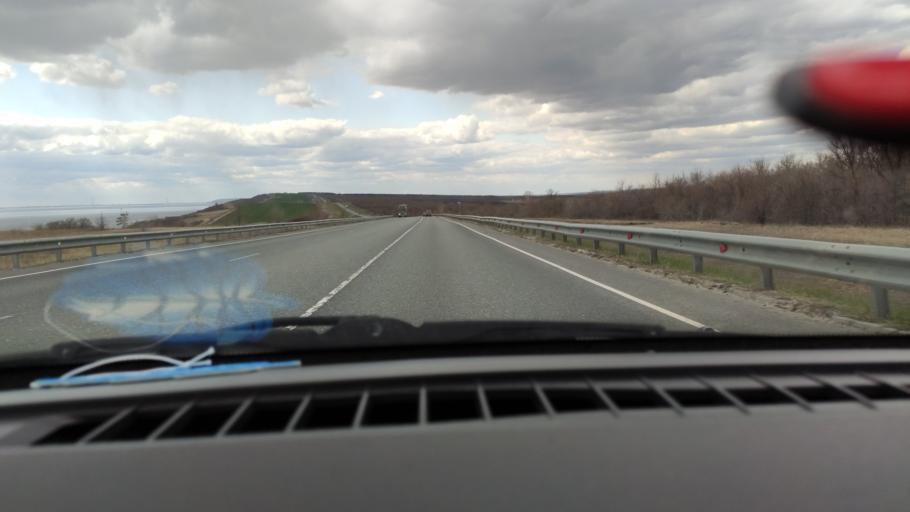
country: RU
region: Saratov
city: Balakovo
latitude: 52.1990
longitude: 47.8634
